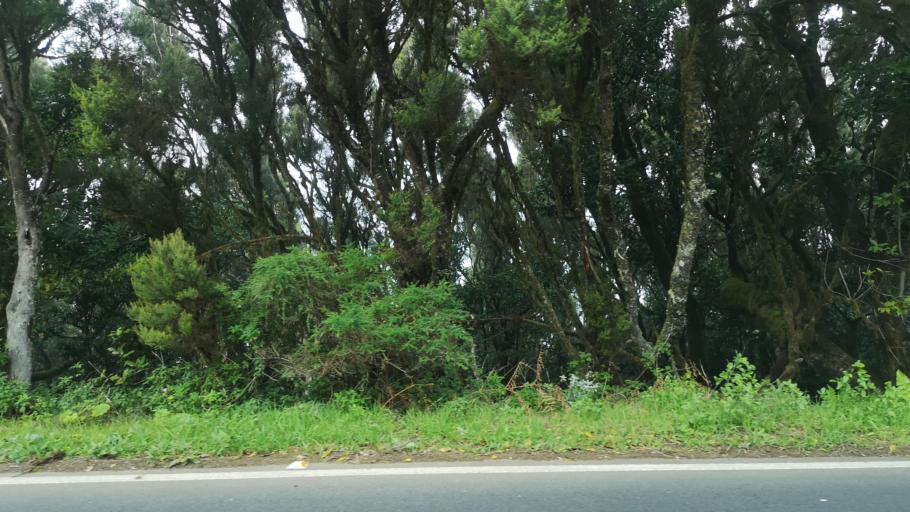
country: ES
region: Canary Islands
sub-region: Provincia de Santa Cruz de Tenerife
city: Alajero
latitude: 28.1069
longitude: -17.2330
